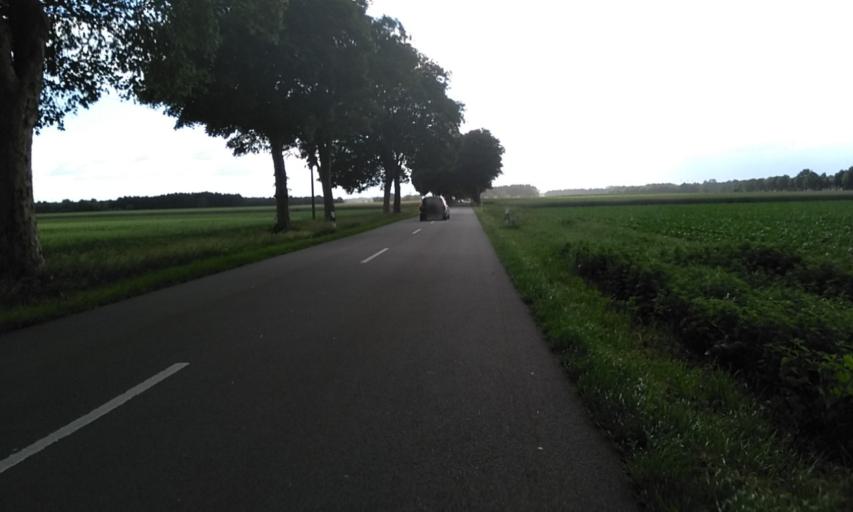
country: DE
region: Lower Saxony
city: Wohnste
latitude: 53.3563
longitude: 9.5135
